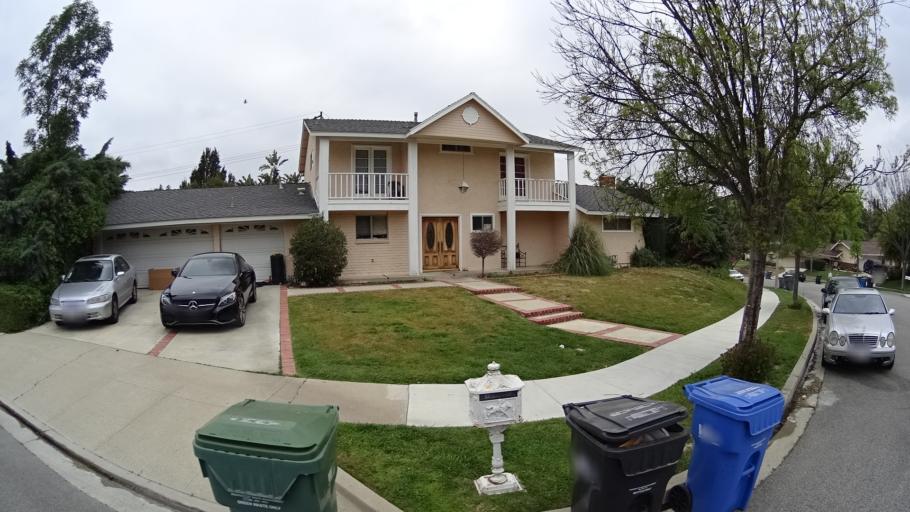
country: US
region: California
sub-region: Ventura County
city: Thousand Oaks
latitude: 34.2053
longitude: -118.8750
